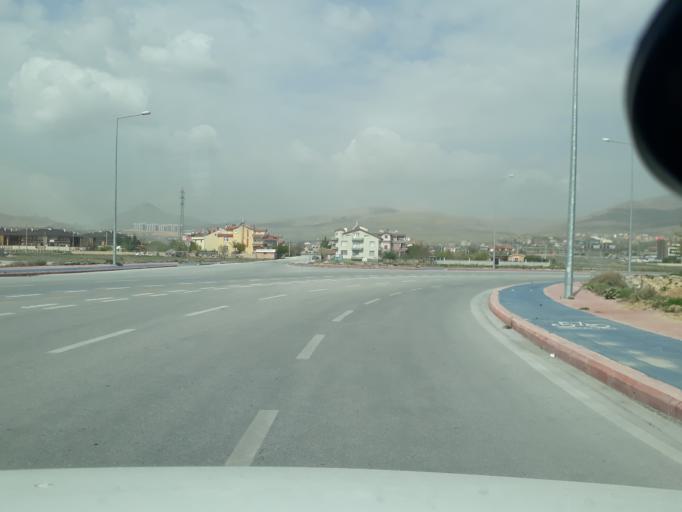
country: TR
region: Konya
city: Selcuklu
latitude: 37.9424
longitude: 32.4824
